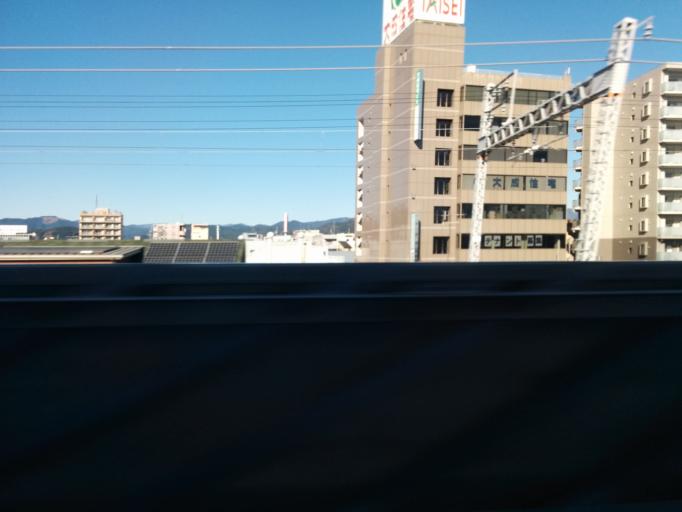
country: JP
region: Shizuoka
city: Shizuoka-shi
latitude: 34.9623
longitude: 138.3769
